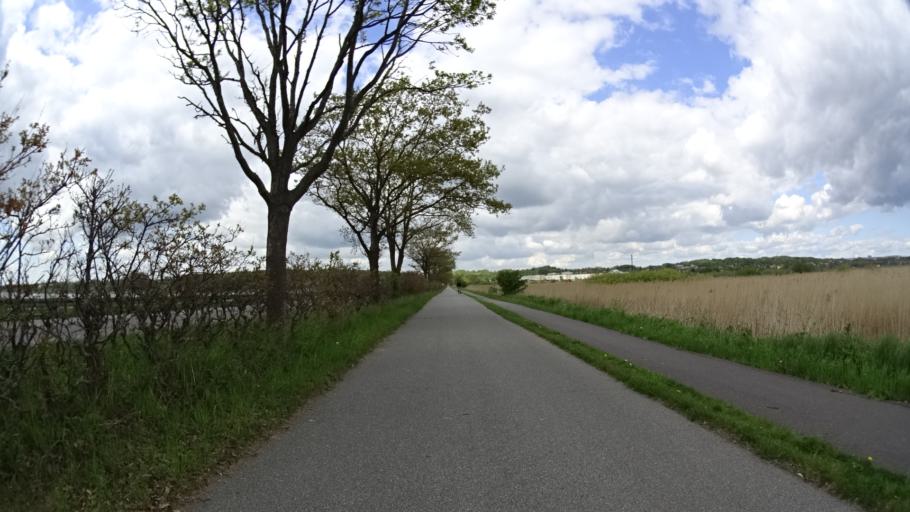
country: DK
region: Central Jutland
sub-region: Arhus Kommune
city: Stavtrup
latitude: 56.1429
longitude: 10.0895
